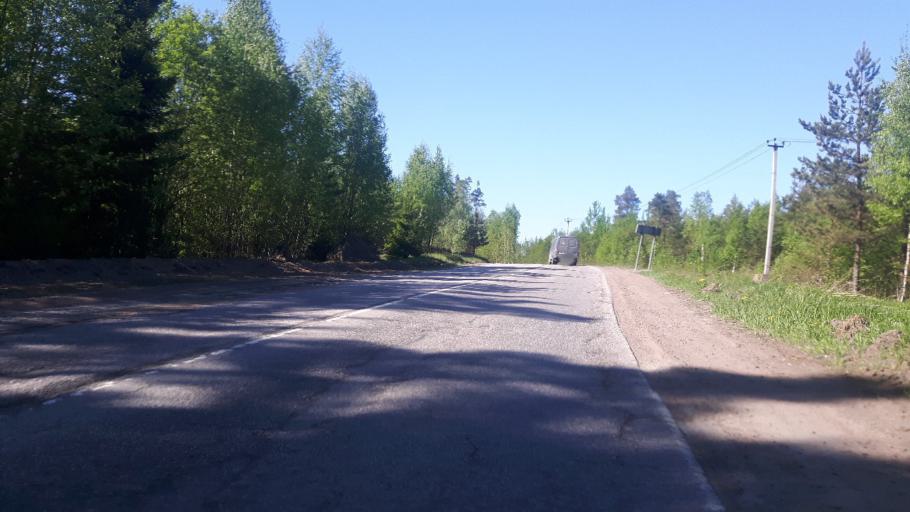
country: RU
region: Leningrad
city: Vyborg
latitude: 60.6473
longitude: 28.7486
